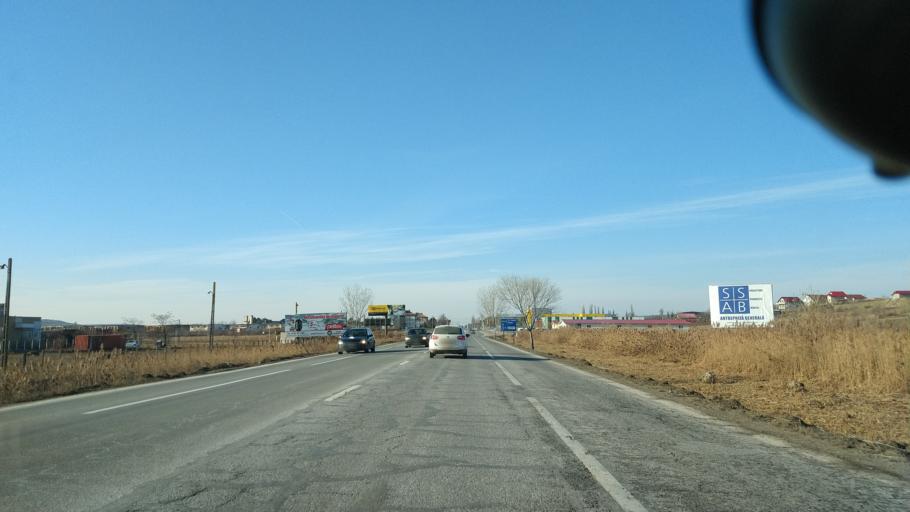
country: RO
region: Iasi
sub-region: Comuna Valea Lupului
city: Valea Lupului
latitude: 47.1840
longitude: 27.4586
